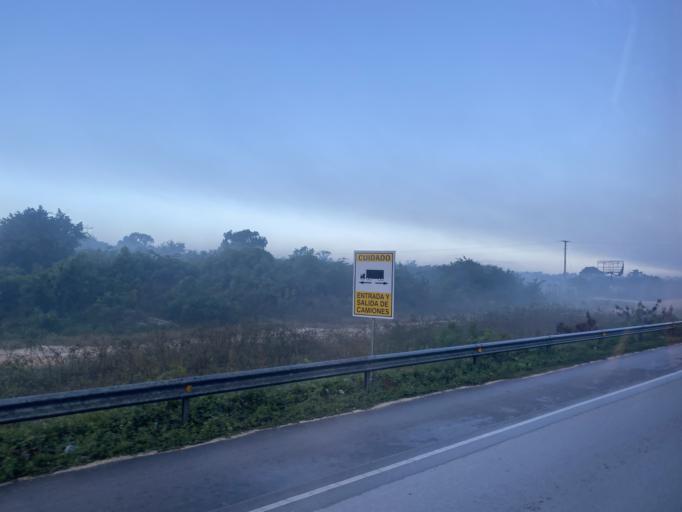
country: DO
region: La Altagracia
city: Otra Banda
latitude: 18.7317
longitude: -68.5042
